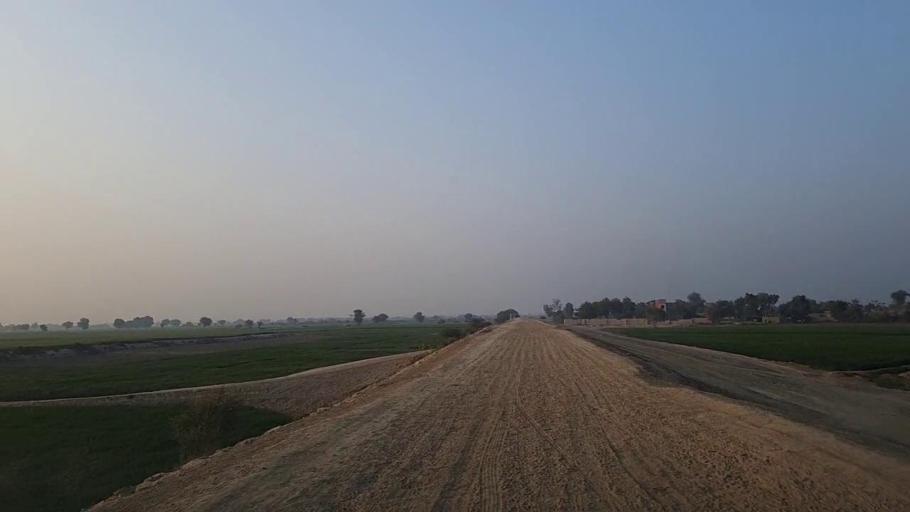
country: PK
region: Sindh
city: Sann
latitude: 26.1913
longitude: 68.0902
